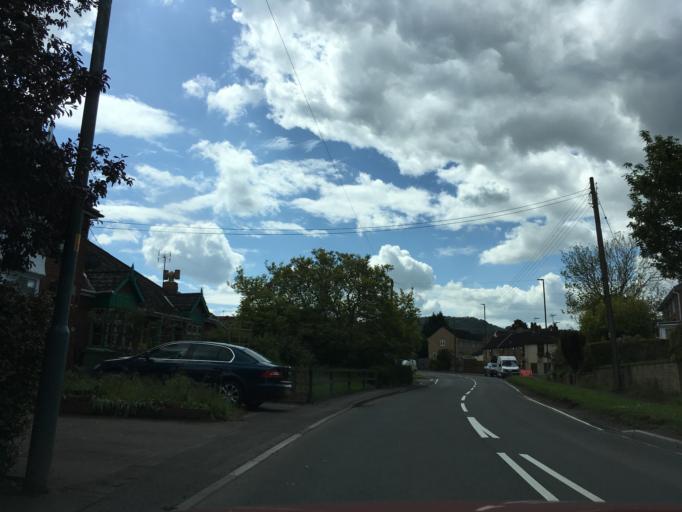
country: GB
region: England
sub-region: Gloucestershire
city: Dursley
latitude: 51.7059
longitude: -2.3663
